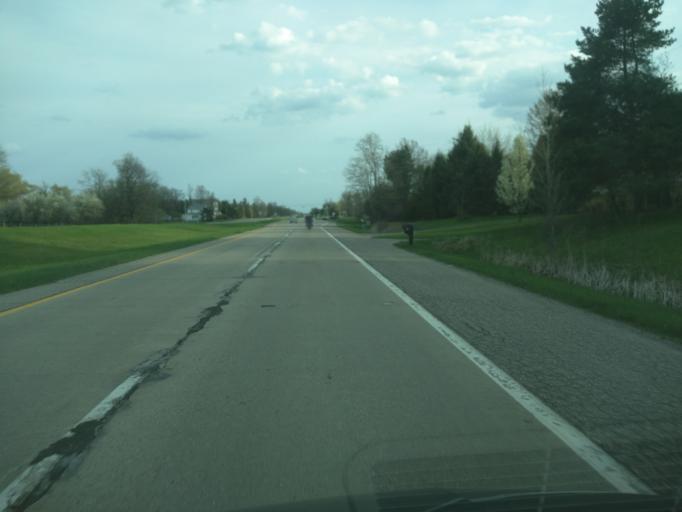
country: US
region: Michigan
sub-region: Eaton County
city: Dimondale
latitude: 42.5842
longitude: -84.6223
